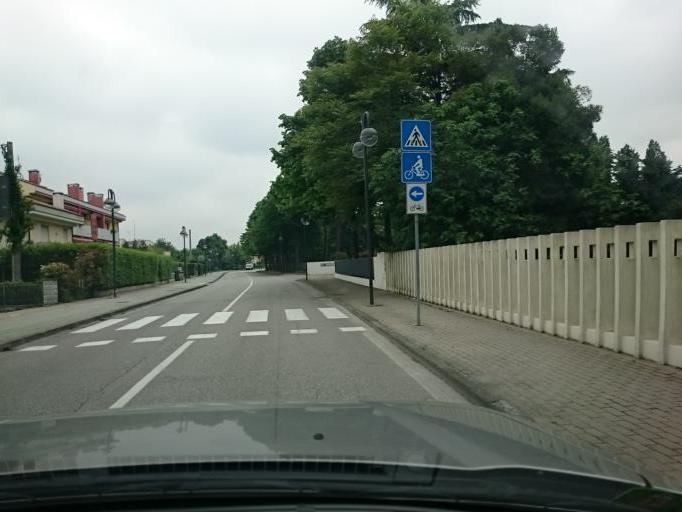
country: IT
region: Veneto
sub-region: Provincia di Padova
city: Montegrotto Terme
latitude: 45.3258
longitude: 11.8001
